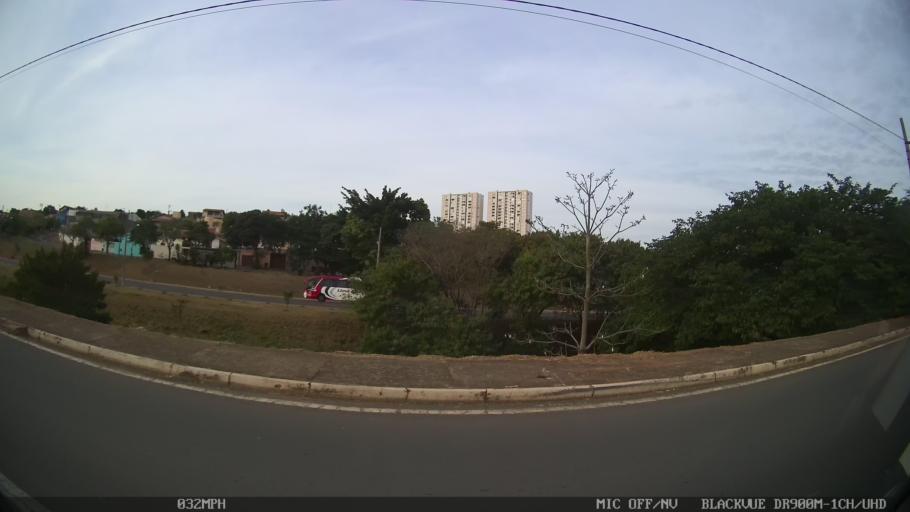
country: BR
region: Sao Paulo
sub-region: Limeira
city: Limeira
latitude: -22.5809
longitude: -47.4122
